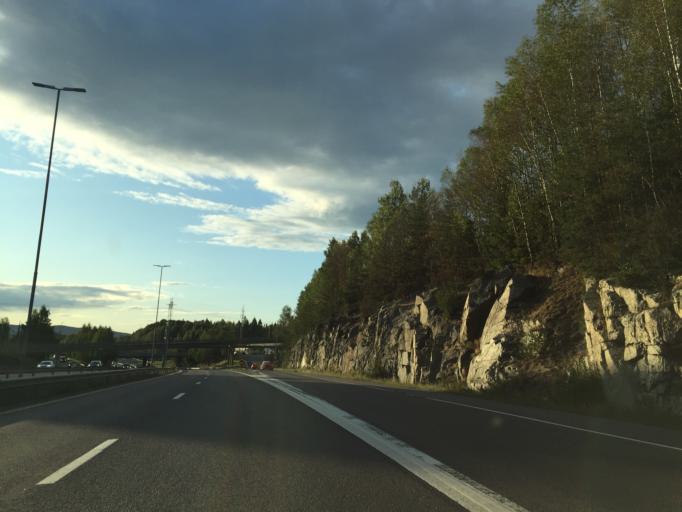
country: NO
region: Akershus
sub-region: Lorenskog
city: Kjenn
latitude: 59.9347
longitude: 10.9400
